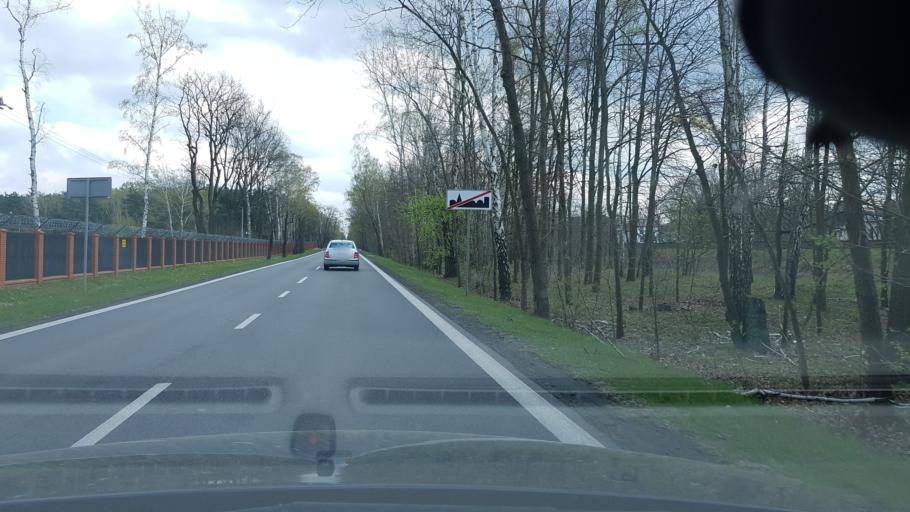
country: PL
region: Masovian Voivodeship
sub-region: Warszawa
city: Wesola
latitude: 52.2539
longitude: 21.2353
